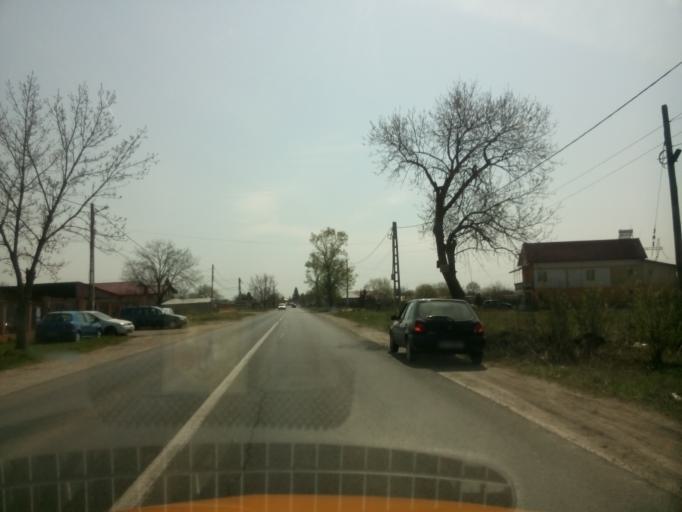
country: RO
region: Calarasi
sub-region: Comuna Frumusani
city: Frumusani
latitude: 44.3043
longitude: 26.3012
